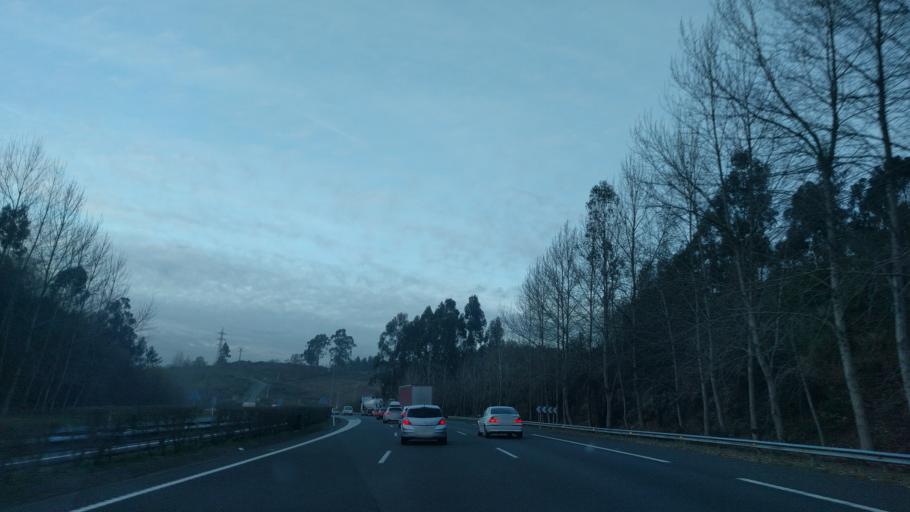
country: ES
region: Cantabria
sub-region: Provincia de Cantabria
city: Barcena de Cicero
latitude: 43.4079
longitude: -3.4971
